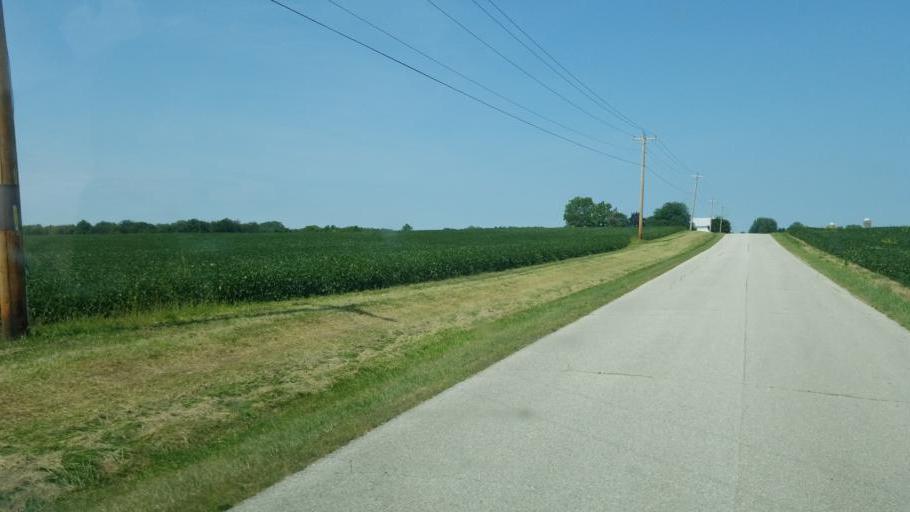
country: US
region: Ohio
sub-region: Crawford County
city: Bucyrus
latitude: 40.8558
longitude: -83.1124
